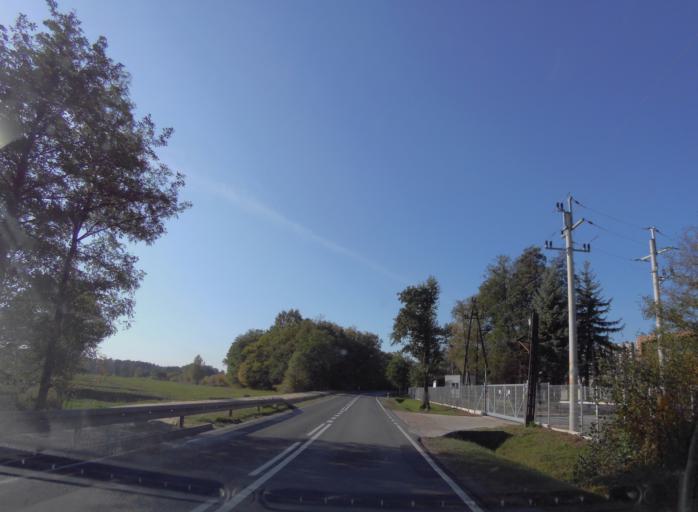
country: PL
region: Masovian Voivodeship
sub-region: Powiat minski
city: Halinow
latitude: 52.1988
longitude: 21.3766
